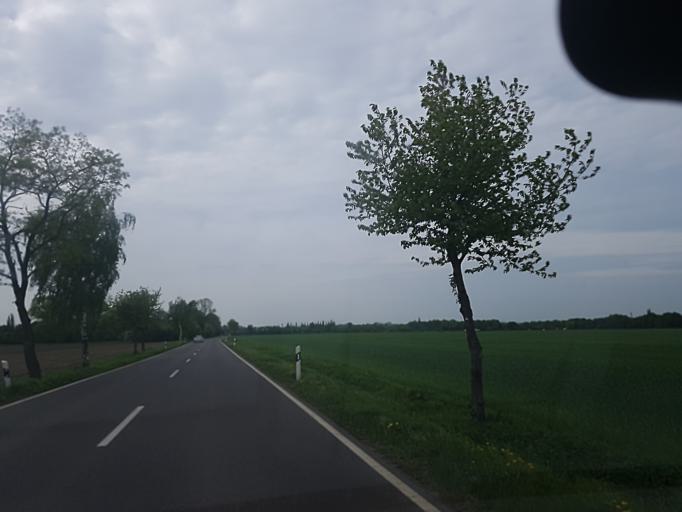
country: DE
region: Brandenburg
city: Finsterwalde
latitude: 51.6198
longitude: 13.7368
